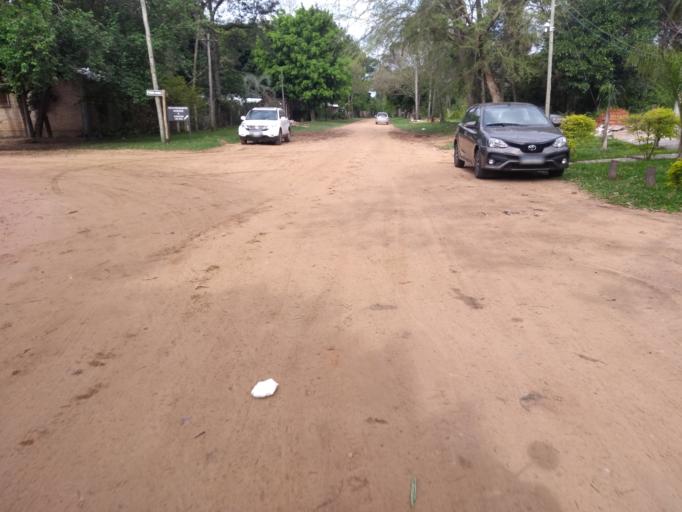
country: AR
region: Corrientes
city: San Luis del Palmar
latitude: -27.4586
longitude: -58.6601
